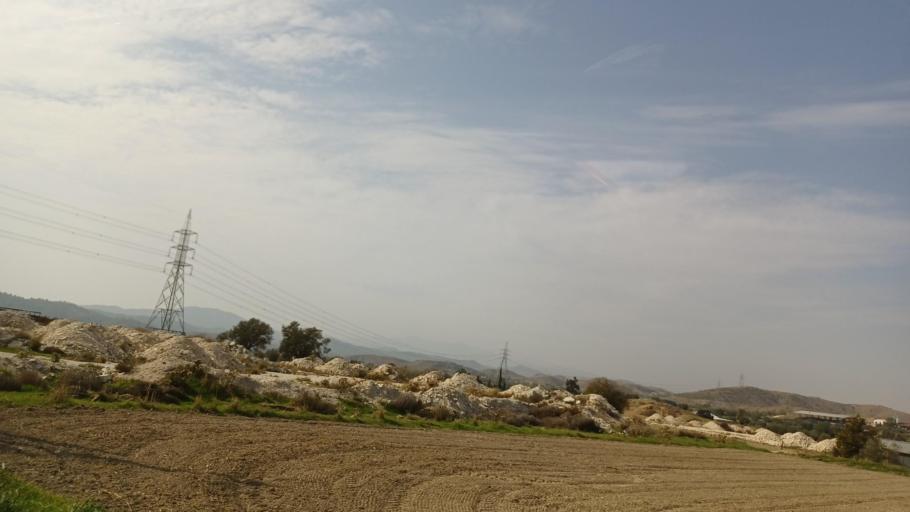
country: CY
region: Lefkosia
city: Lympia
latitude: 34.9837
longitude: 33.4535
